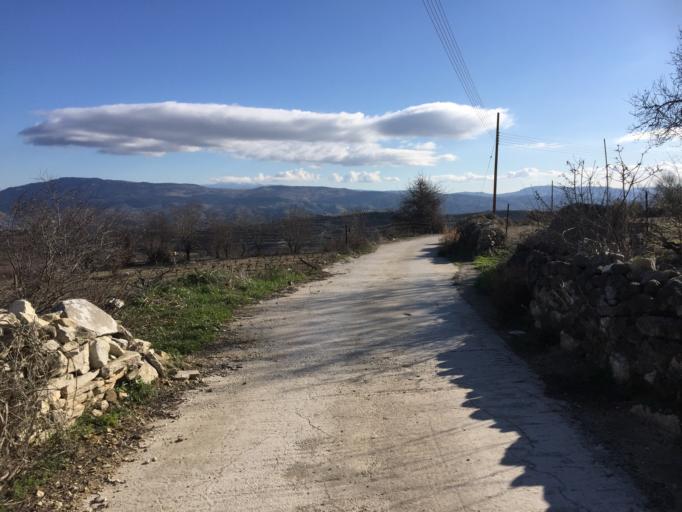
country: CY
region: Pafos
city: Mesogi
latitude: 34.8416
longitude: 32.5082
